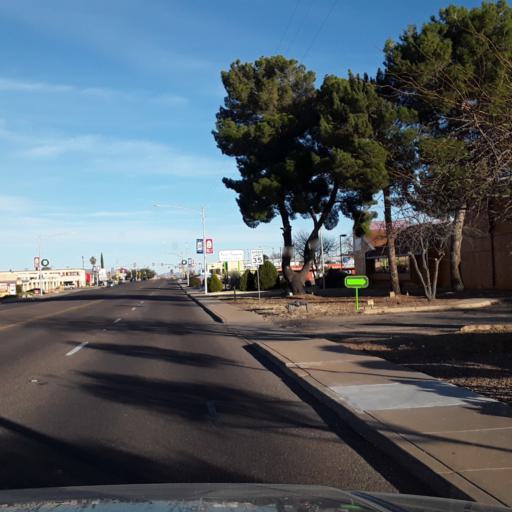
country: US
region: Arizona
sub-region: Cochise County
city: Sierra Vista
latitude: 31.5543
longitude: -110.3041
